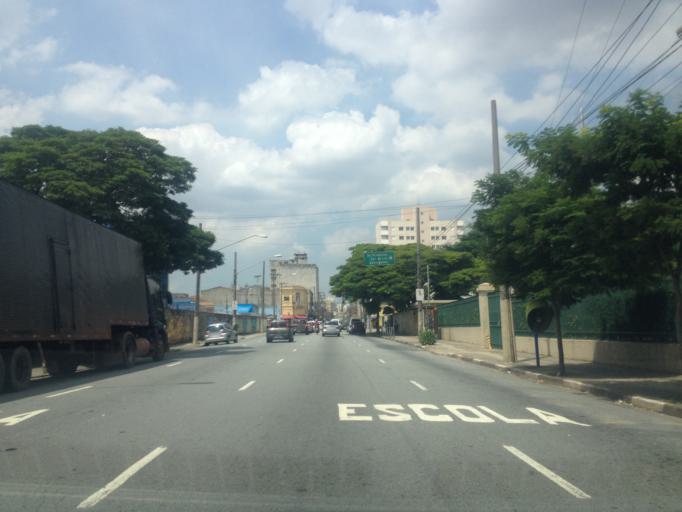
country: BR
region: Sao Paulo
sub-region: Sao Paulo
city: Sao Paulo
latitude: -23.5327
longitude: -46.6262
